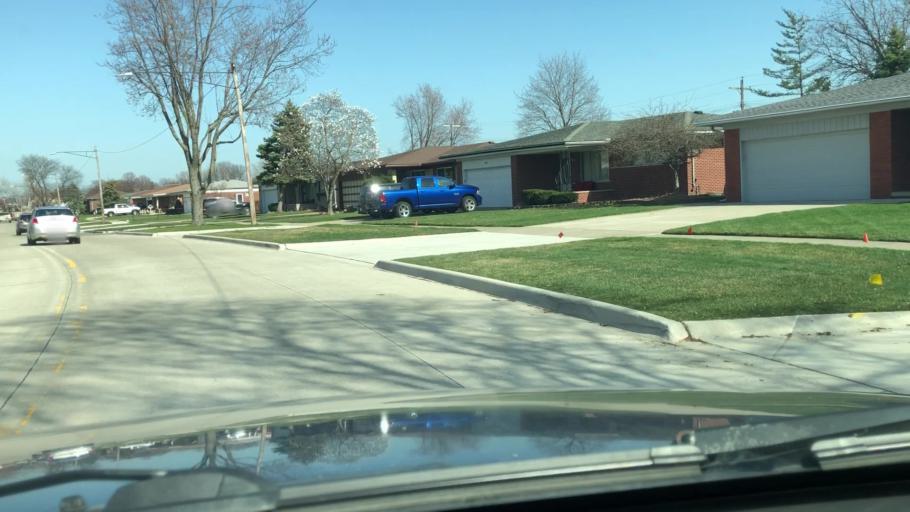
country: US
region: Michigan
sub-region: Macomb County
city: Center Line
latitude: 42.4998
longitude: -82.9904
